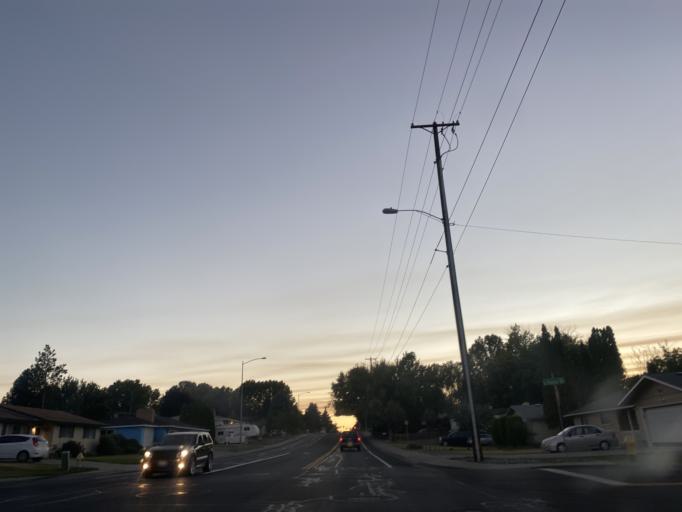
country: US
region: Washington
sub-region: Benton County
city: Kennewick
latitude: 46.1986
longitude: -119.1429
